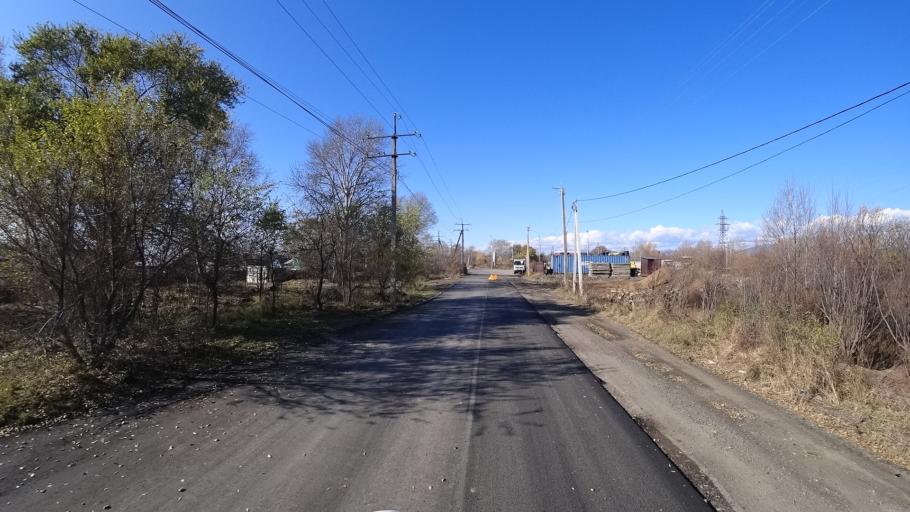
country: RU
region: Khabarovsk Krai
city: Amursk
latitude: 50.1053
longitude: 136.5146
